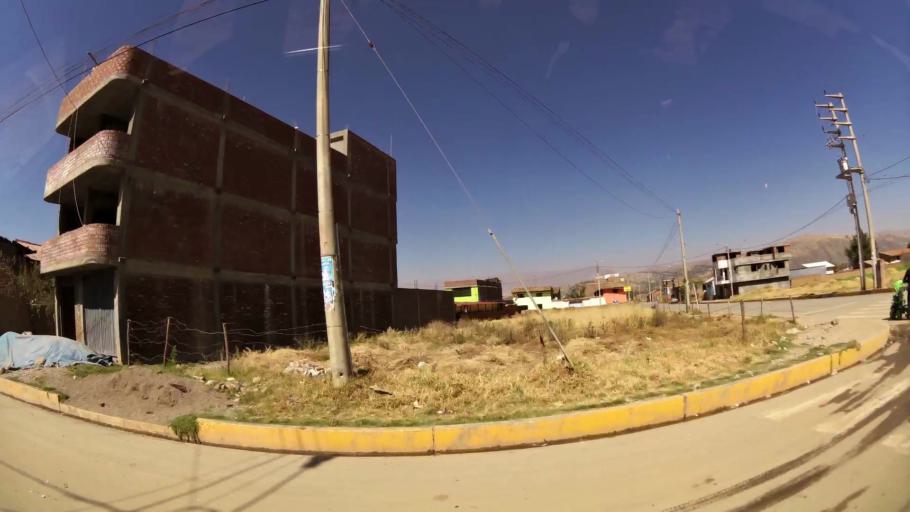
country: PE
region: Junin
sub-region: Provincia de Huancayo
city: San Jeronimo
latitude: -11.9424
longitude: -75.2934
